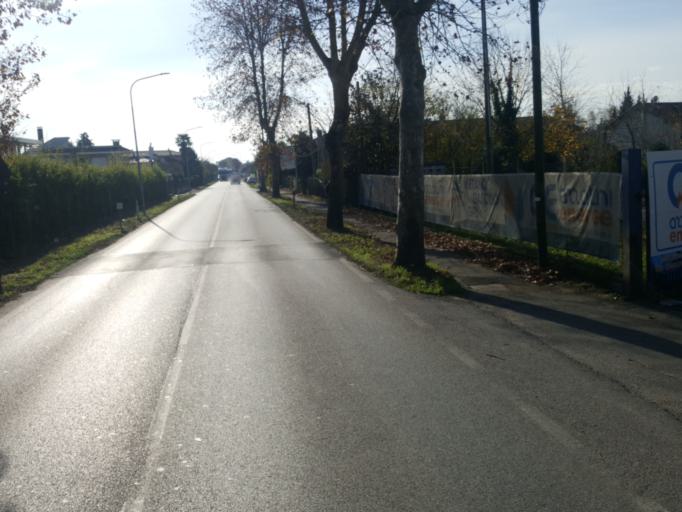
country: IT
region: Veneto
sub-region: Provincia di Treviso
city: Castelfranco Veneto
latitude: 45.6868
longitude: 11.9274
